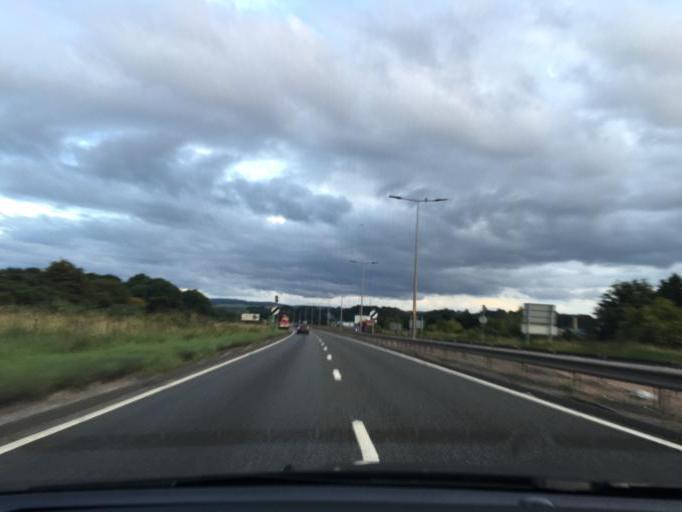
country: GB
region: Scotland
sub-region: Highland
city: Inverness
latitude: 57.4886
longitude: -4.2099
